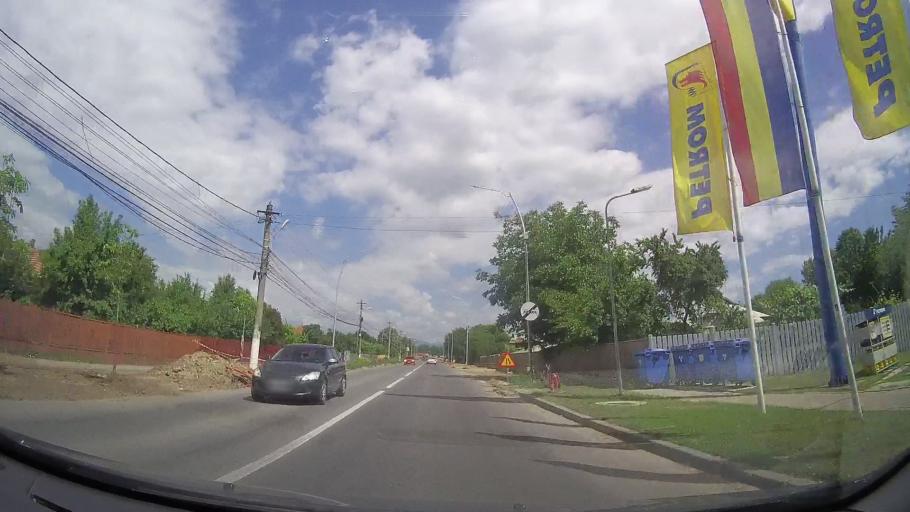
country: RO
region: Prahova
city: Drajna de Jos
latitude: 45.2007
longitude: 26.0437
